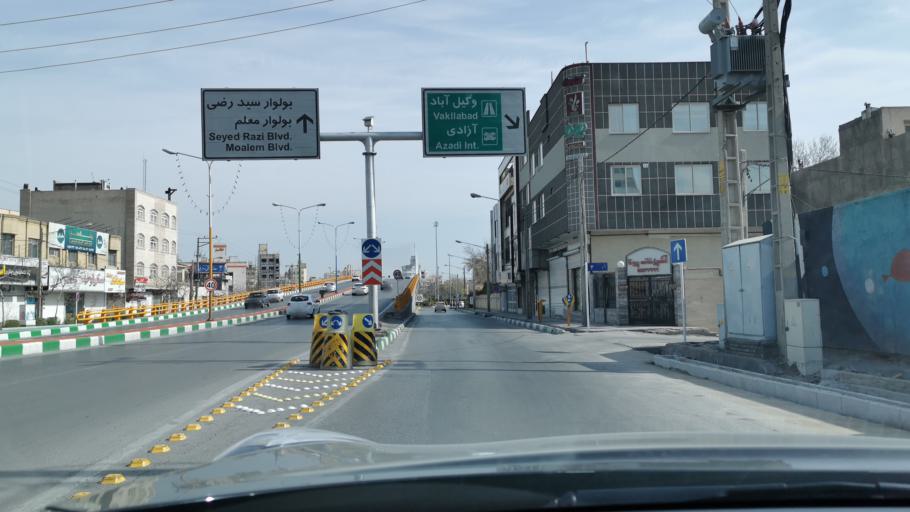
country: IR
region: Razavi Khorasan
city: Mashhad
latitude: 36.3212
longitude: 59.5141
